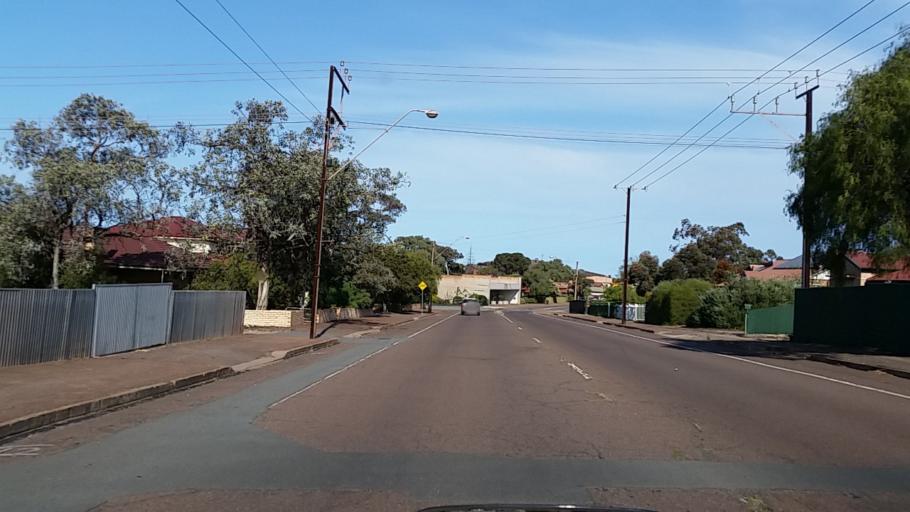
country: AU
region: South Australia
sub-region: Whyalla
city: Whyalla
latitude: -33.0301
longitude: 137.5801
